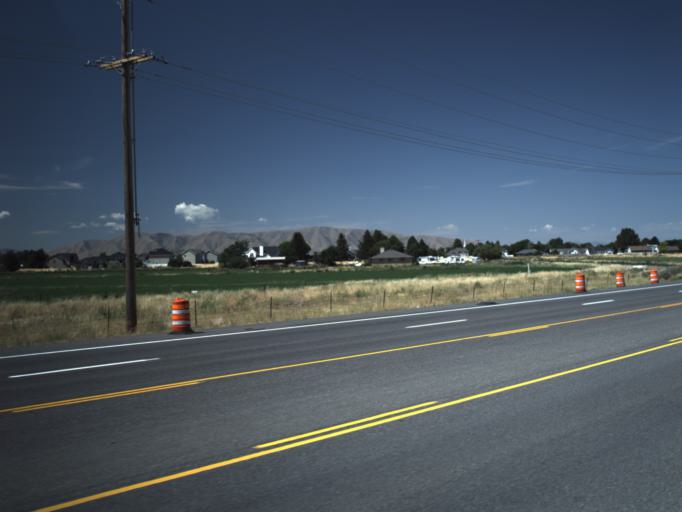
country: US
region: Utah
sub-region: Utah County
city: Spanish Fork
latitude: 40.1003
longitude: -111.6141
